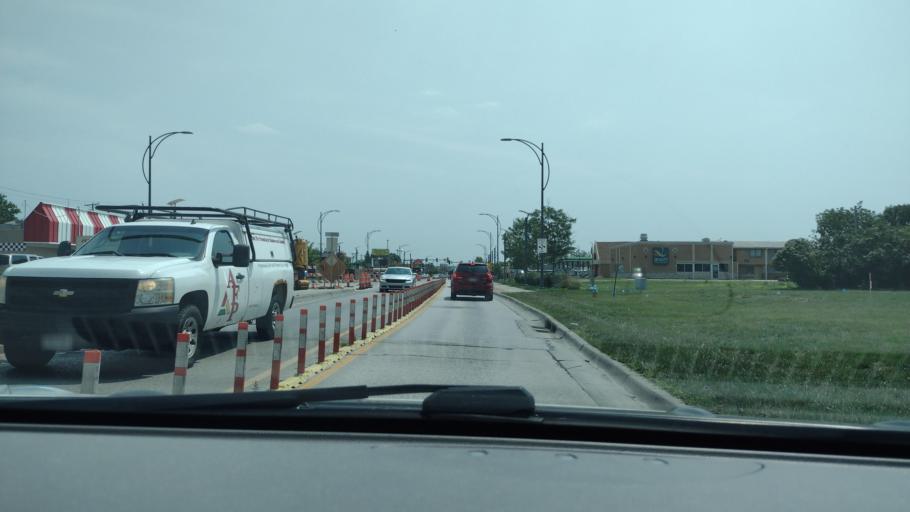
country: US
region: Iowa
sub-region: Pottawattamie County
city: Carter Lake
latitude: 41.2619
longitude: -95.9050
